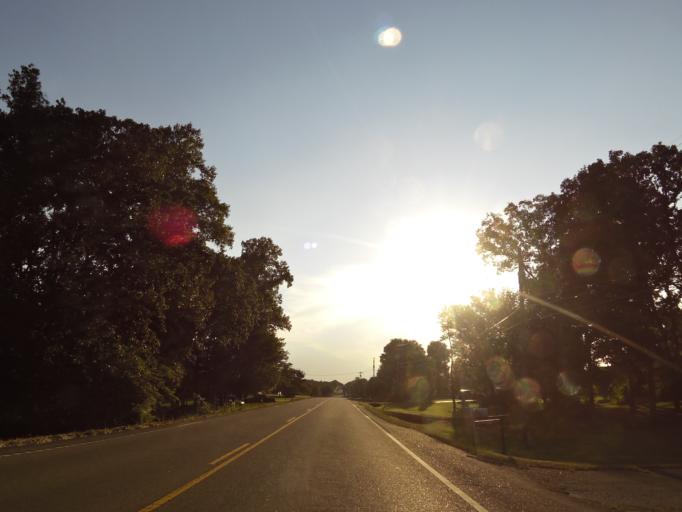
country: US
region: Tennessee
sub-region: McMinn County
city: Englewood
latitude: 35.4256
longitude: -84.5245
